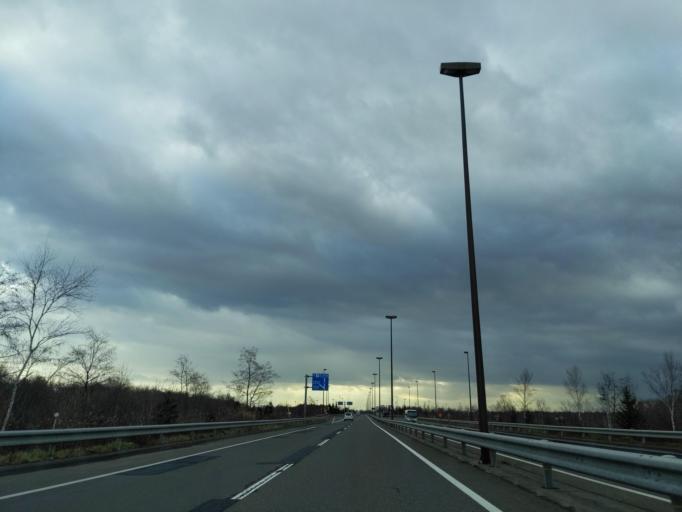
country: JP
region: Hokkaido
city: Chitose
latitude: 42.8218
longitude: 141.6852
